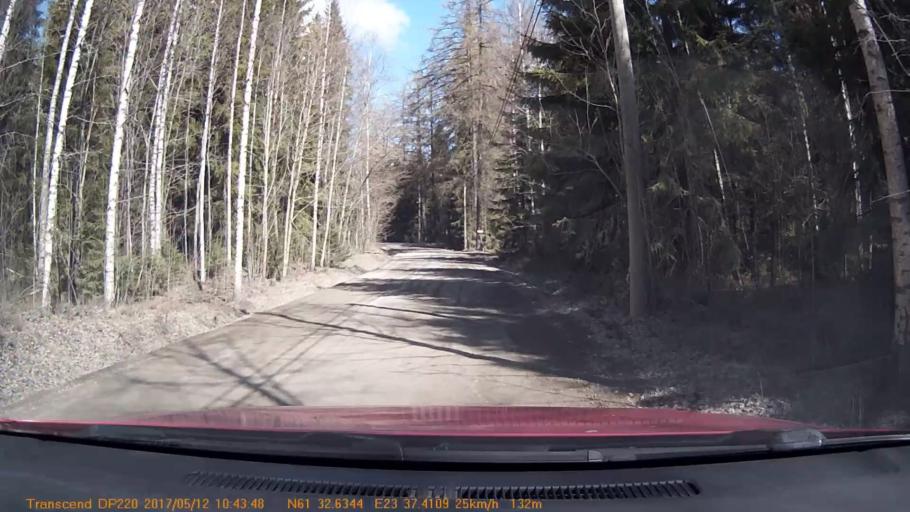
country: FI
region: Pirkanmaa
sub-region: Tampere
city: Yloejaervi
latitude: 61.5438
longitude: 23.6233
